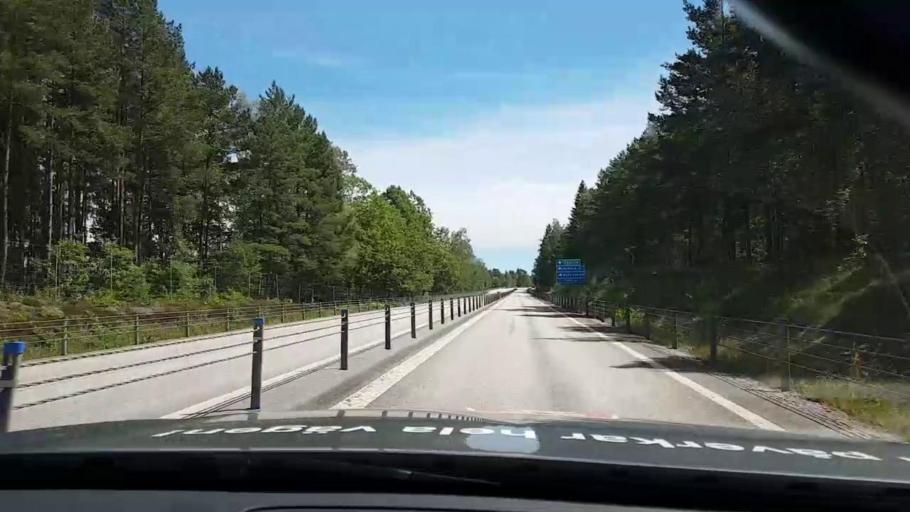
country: SE
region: Kalmar
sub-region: Vasterviks Kommun
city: Gamleby
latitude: 57.8205
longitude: 16.4700
